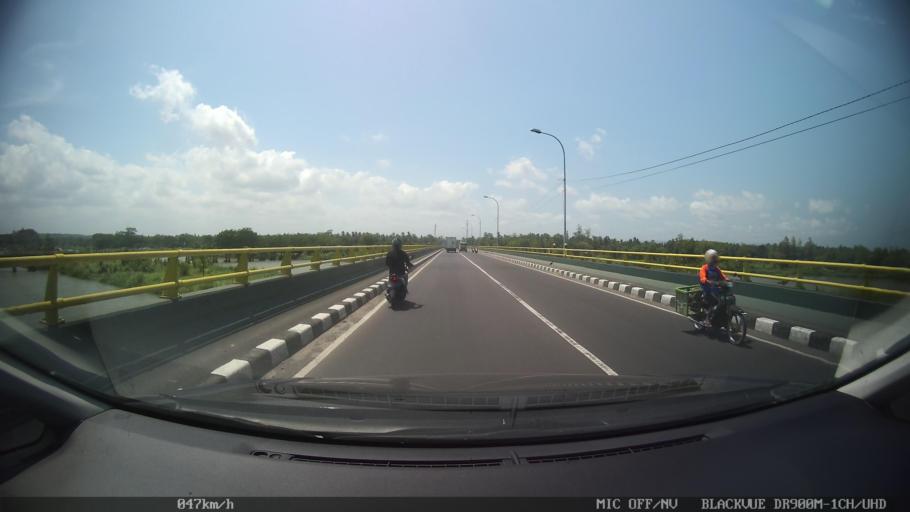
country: ID
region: Daerah Istimewa Yogyakarta
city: Srandakan
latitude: -7.9396
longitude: 110.2408
